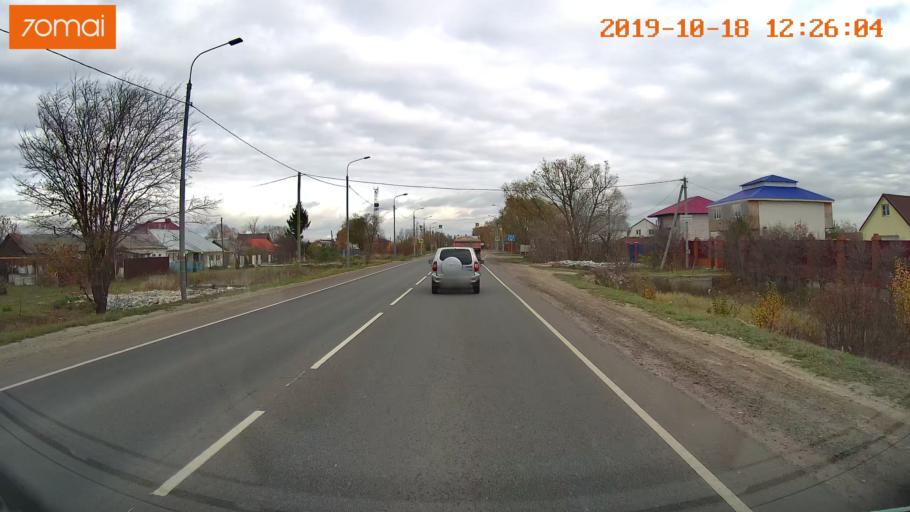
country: RU
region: Rjazan
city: Rybnoye
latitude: 54.5550
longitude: 39.5283
